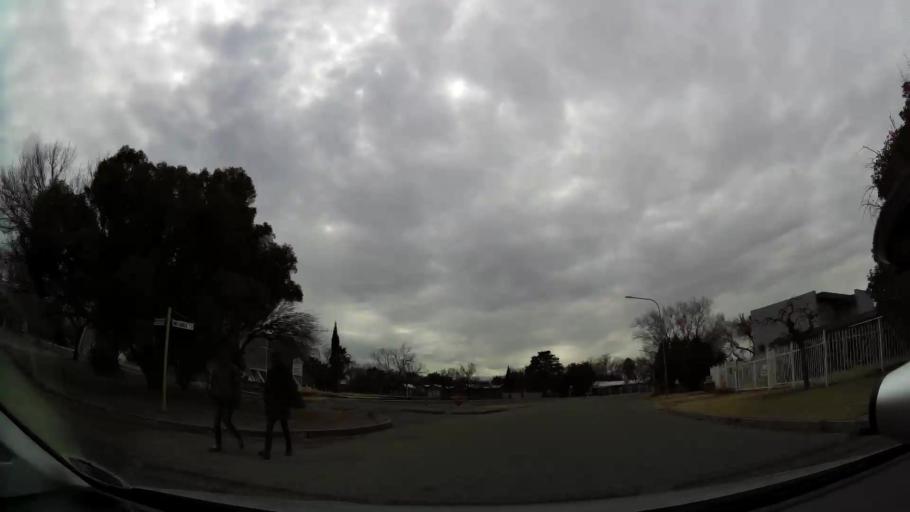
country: ZA
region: Orange Free State
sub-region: Fezile Dabi District Municipality
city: Kroonstad
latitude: -27.6411
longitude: 27.2374
